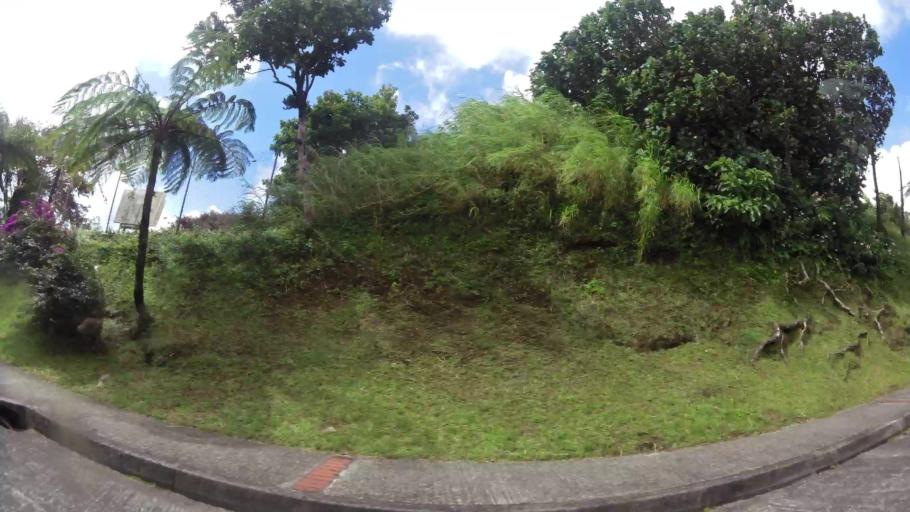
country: MQ
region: Martinique
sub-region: Martinique
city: Le Morne-Rouge
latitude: 14.7817
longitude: -61.1365
